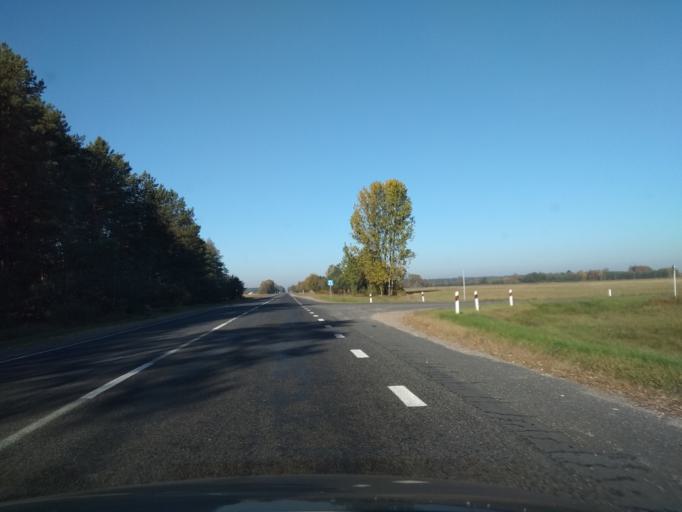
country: BY
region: Brest
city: Malaryta
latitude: 51.9447
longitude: 24.0241
